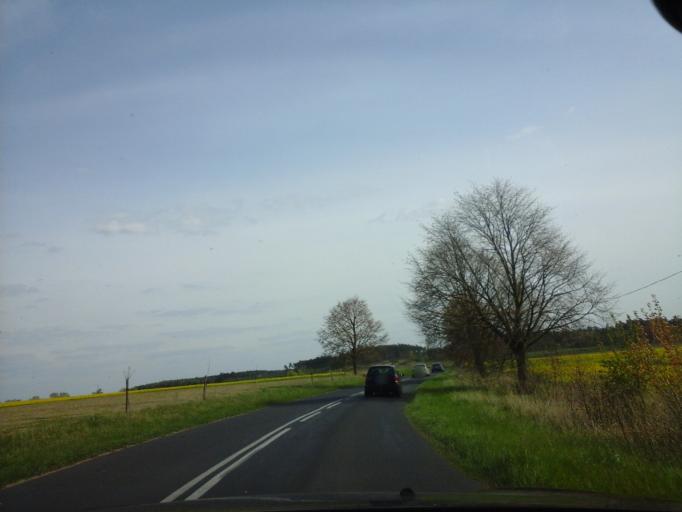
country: PL
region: West Pomeranian Voivodeship
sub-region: Powiat choszczenski
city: Krzecin
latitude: 53.0959
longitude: 15.4693
